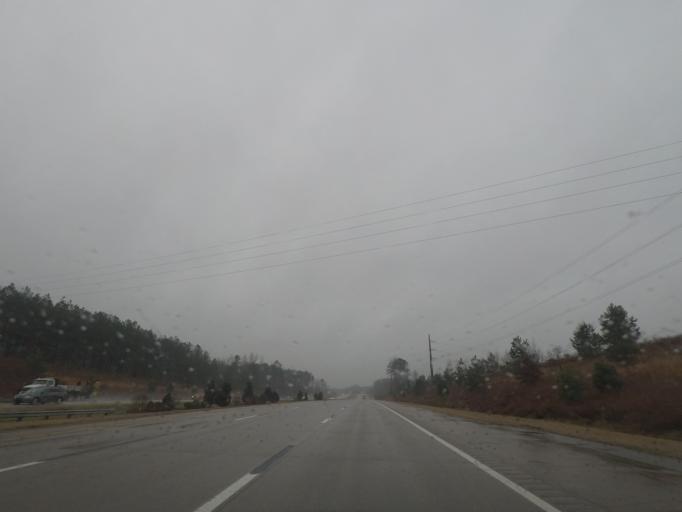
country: US
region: North Carolina
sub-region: Wake County
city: Green Level
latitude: 35.7671
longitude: -78.8871
